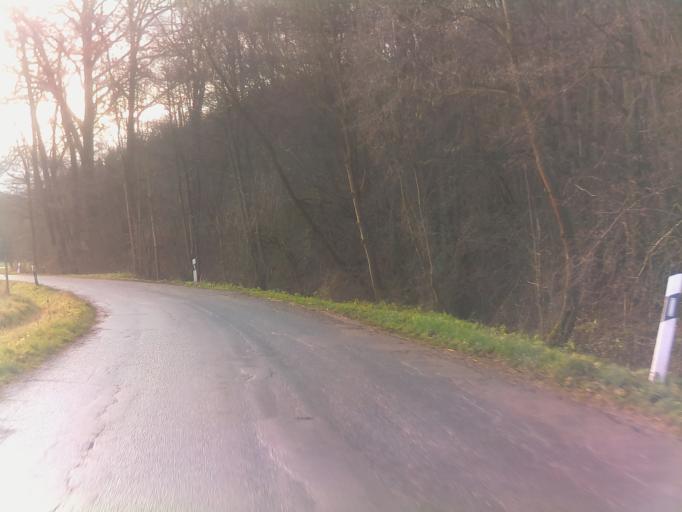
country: DE
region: Thuringia
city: Rottenbach
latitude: 50.7138
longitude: 11.1984
